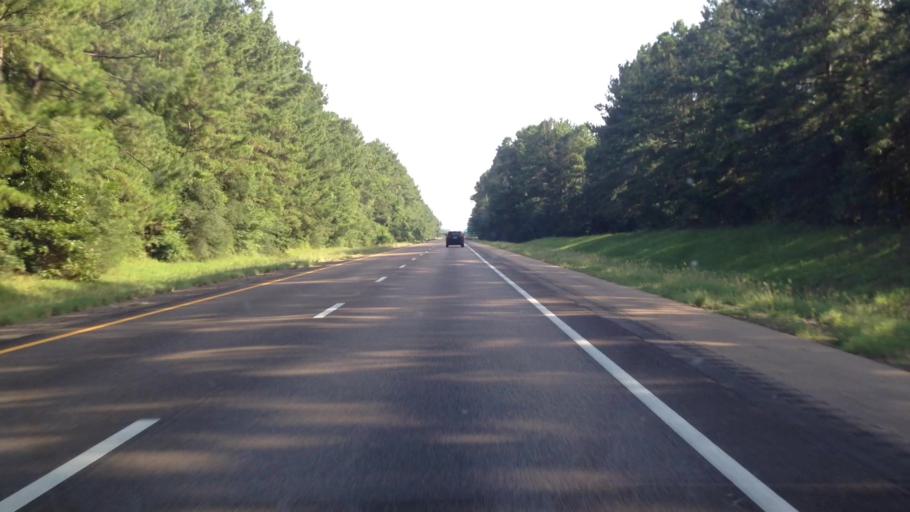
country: US
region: Mississippi
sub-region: Pike County
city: Summit
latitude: 31.3413
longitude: -90.4779
